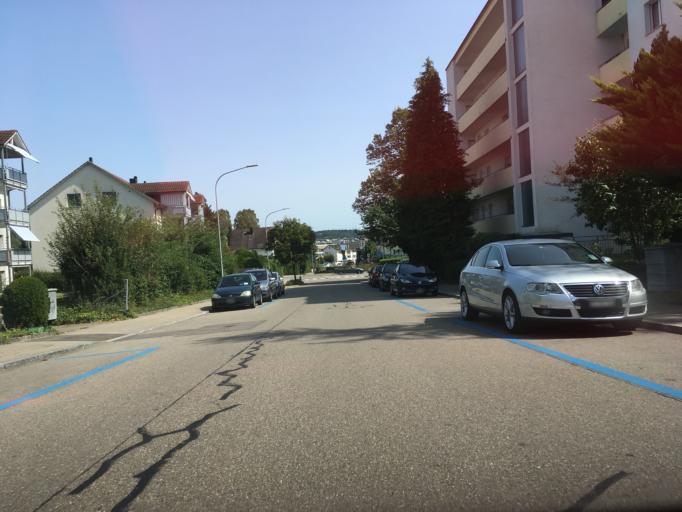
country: CH
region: Zurich
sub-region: Bezirk Buelach
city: Dietlikon / Eichwiesen
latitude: 47.4274
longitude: 8.6176
